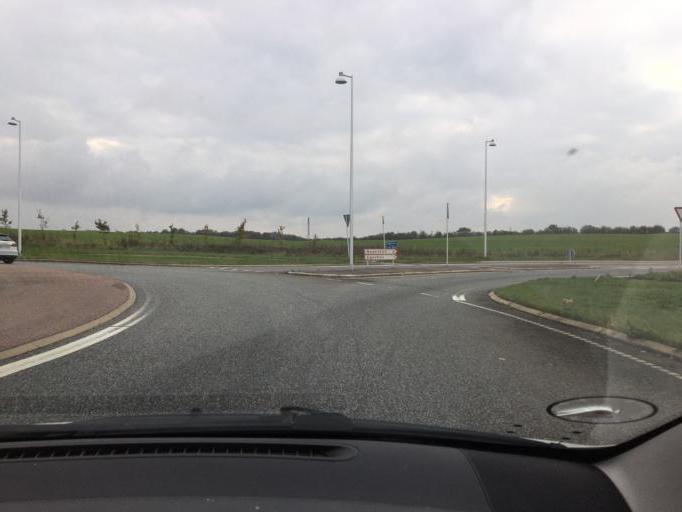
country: DK
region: South Denmark
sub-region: Fredericia Kommune
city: Fredericia
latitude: 55.6082
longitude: 9.7555
